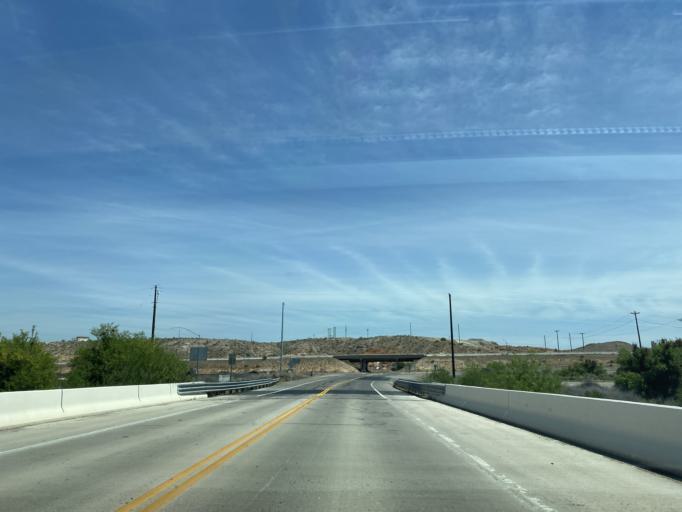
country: US
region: Nevada
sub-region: Clark County
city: Moapa Town
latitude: 36.6620
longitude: -114.5763
